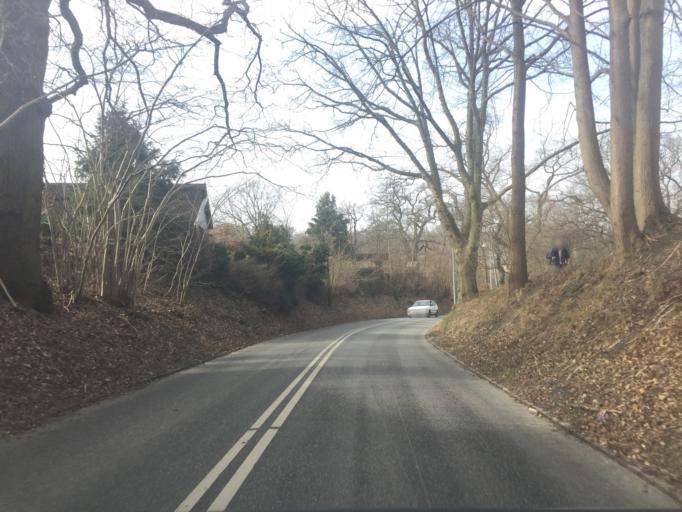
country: DK
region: Capital Region
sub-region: Lyngby-Tarbaek Kommune
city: Kongens Lyngby
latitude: 55.7934
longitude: 12.5027
